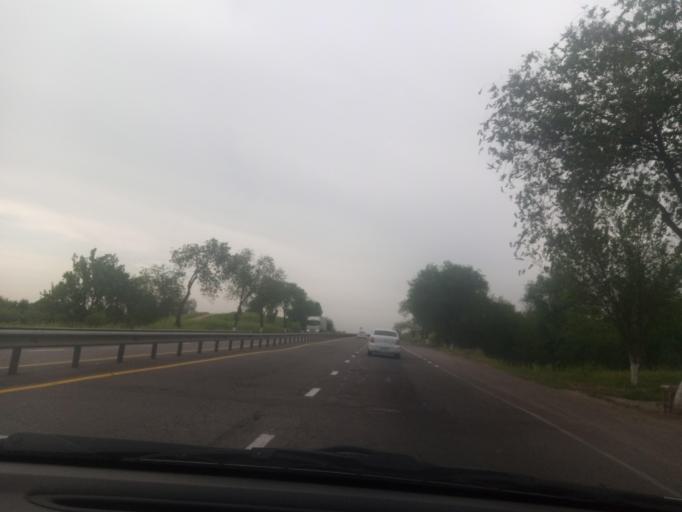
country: UZ
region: Toshkent
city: Tuytepa
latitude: 41.0847
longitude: 69.4670
